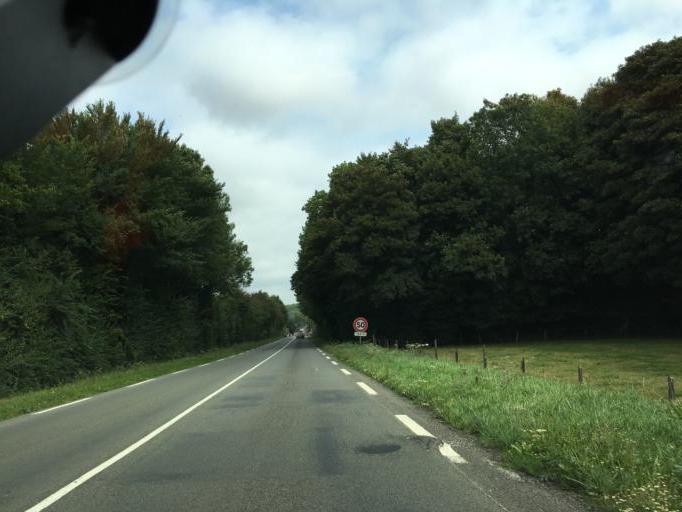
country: FR
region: Nord-Pas-de-Calais
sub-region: Departement du Pas-de-Calais
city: Camblain-Chatelain
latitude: 50.4305
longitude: 2.4437
